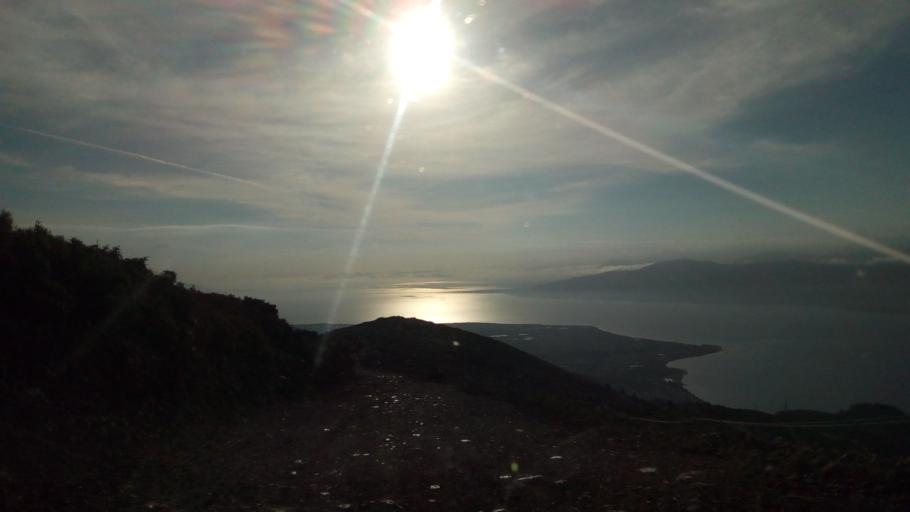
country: GR
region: West Greece
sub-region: Nomos Aitolias kai Akarnanias
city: Nafpaktos
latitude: 38.4164
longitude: 21.8113
